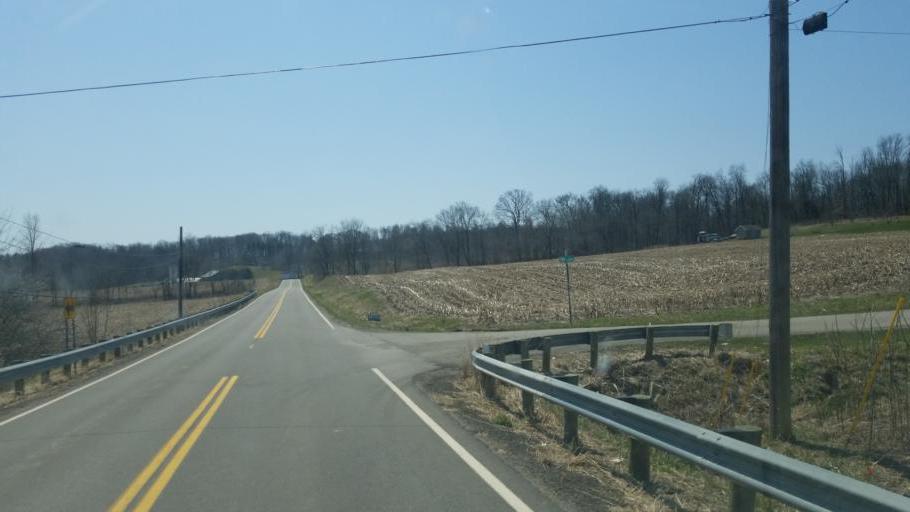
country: US
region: Ohio
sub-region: Ashland County
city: Loudonville
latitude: 40.6827
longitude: -82.2888
